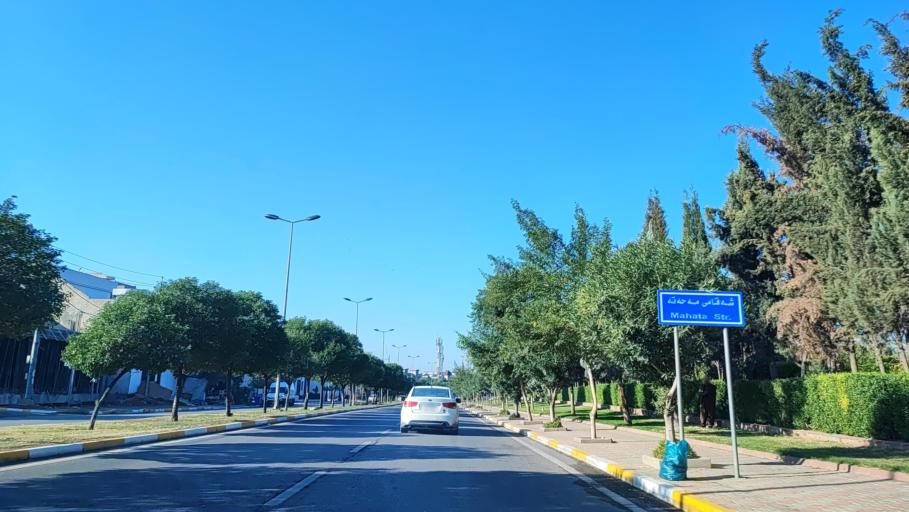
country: IQ
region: Arbil
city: Erbil
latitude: 36.1800
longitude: 44.0065
